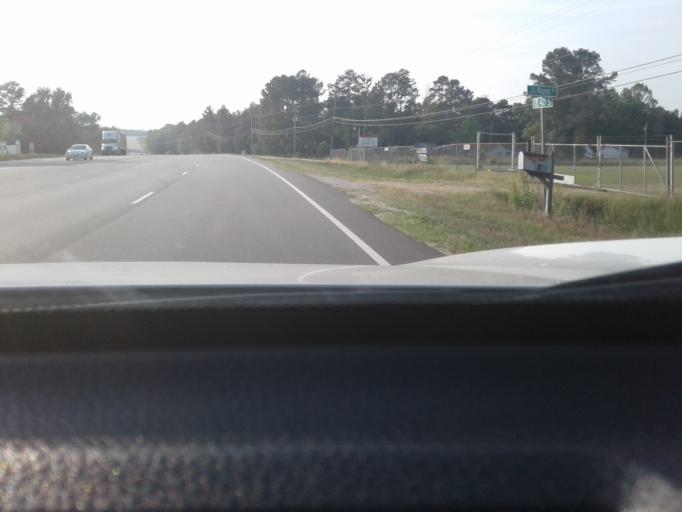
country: US
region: North Carolina
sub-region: Harnett County
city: Buies Creek
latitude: 35.3790
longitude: -78.7137
